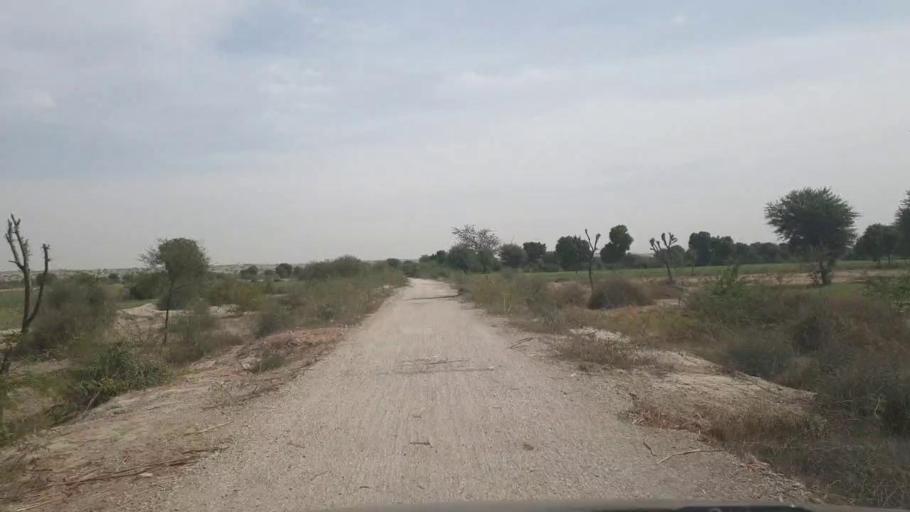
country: PK
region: Sindh
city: Kunri
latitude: 25.1917
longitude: 69.6956
